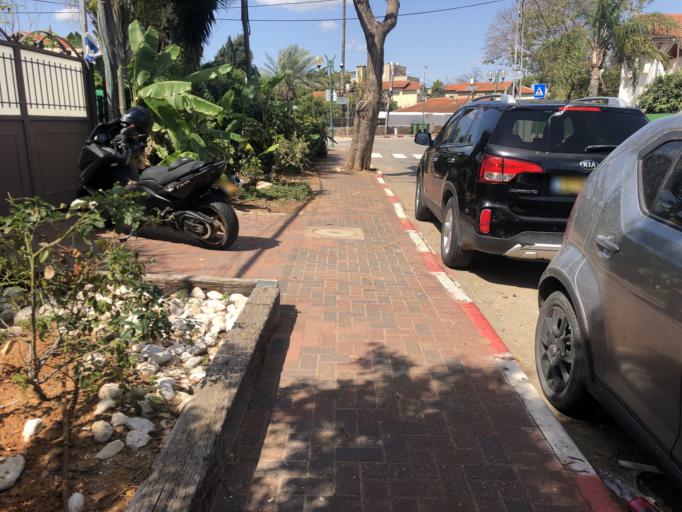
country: IL
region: Central District
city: Kfar Saba
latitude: 32.1581
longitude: 34.9218
